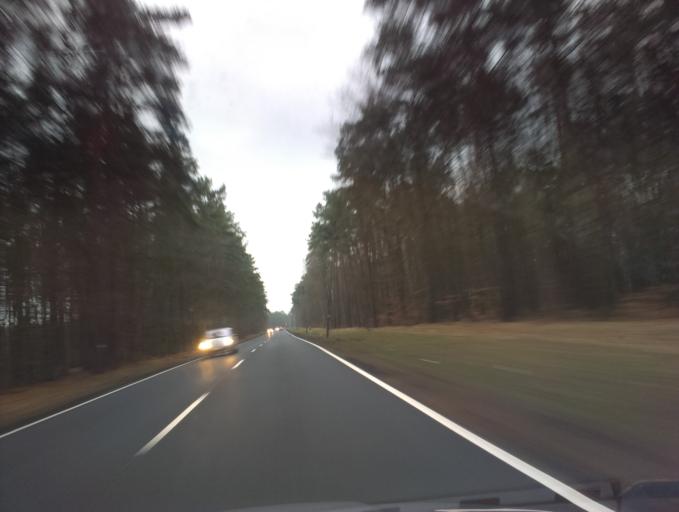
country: PL
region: Greater Poland Voivodeship
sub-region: Powiat zlotowski
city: Tarnowka
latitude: 53.3575
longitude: 16.7864
